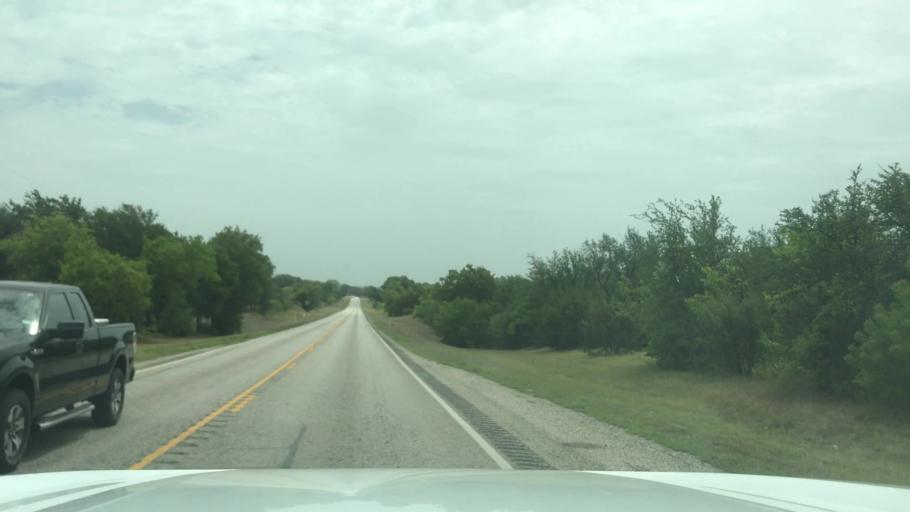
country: US
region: Texas
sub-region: Hamilton County
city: Hico
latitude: 32.0424
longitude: -98.1343
